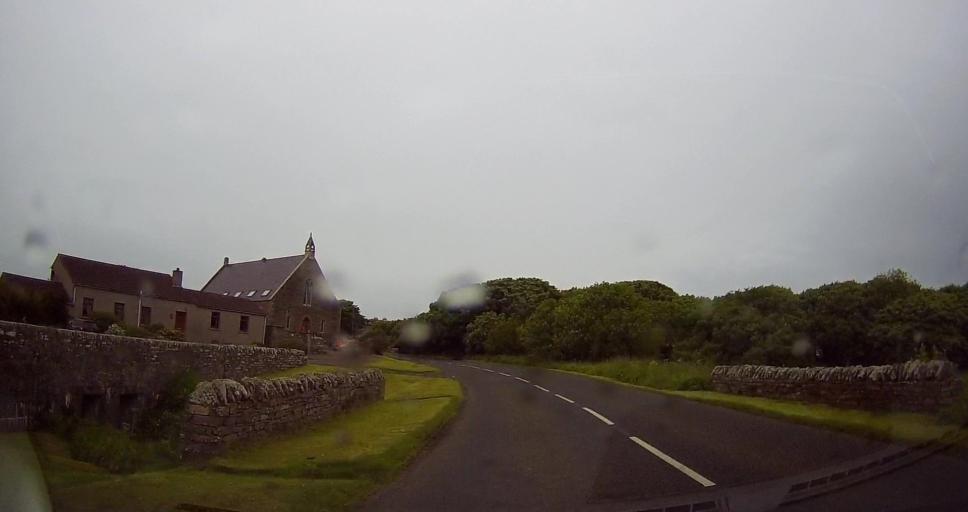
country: GB
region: Scotland
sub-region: Orkney Islands
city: Orkney
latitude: 59.1124
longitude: -3.1046
